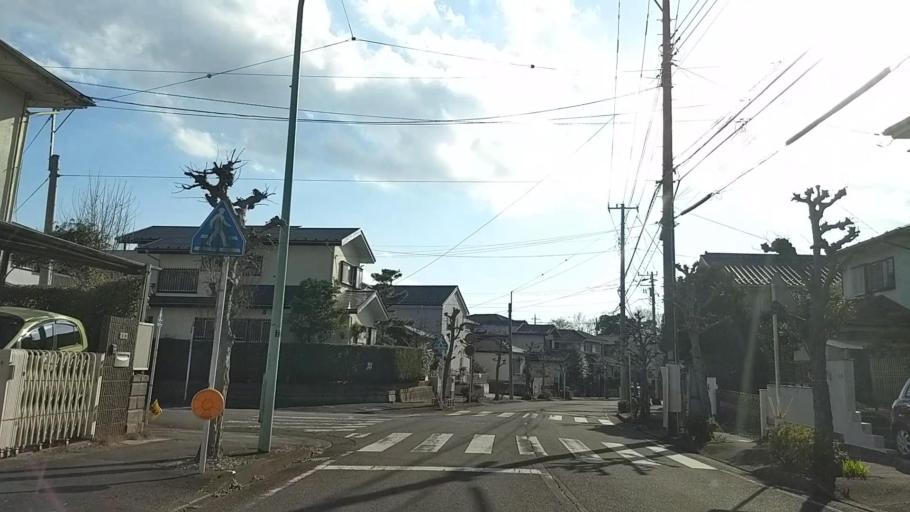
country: JP
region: Kanagawa
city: Atsugi
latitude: 35.4372
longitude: 139.3286
